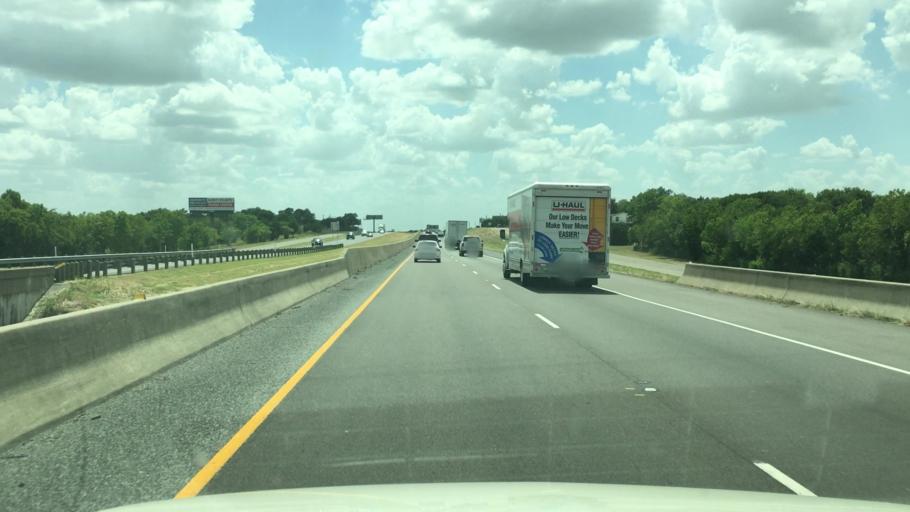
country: US
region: Texas
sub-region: Hunt County
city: Caddo Mills
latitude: 33.0565
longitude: -96.1649
